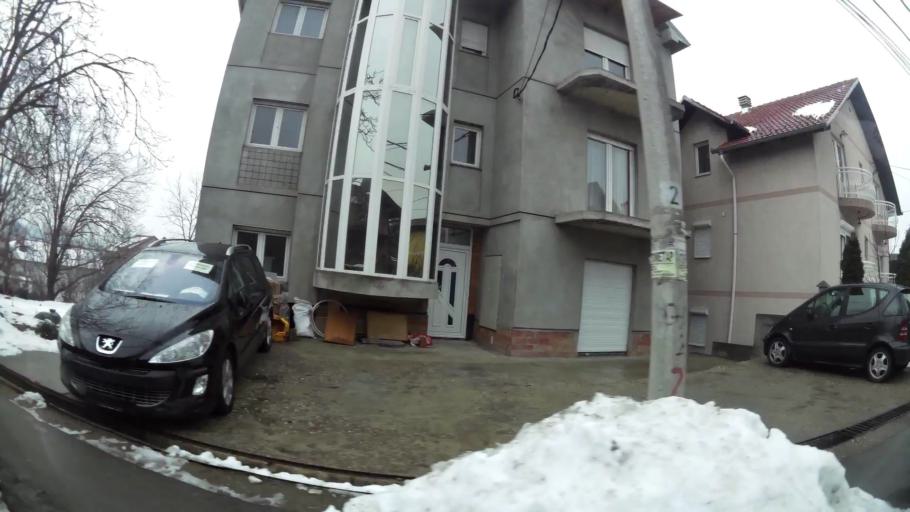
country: RS
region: Central Serbia
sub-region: Belgrade
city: Zvezdara
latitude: 44.7753
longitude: 20.5253
